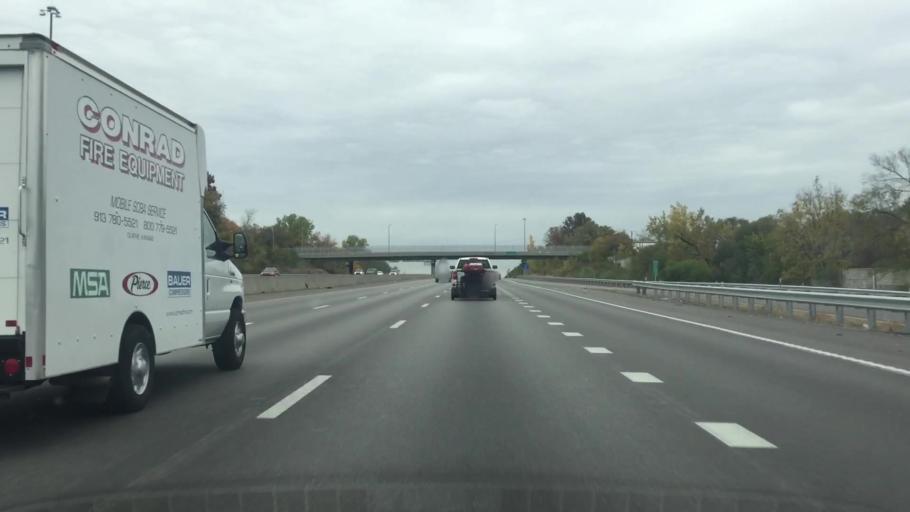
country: US
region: Missouri
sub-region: Jackson County
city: Raytown
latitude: 39.0335
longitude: -94.5002
